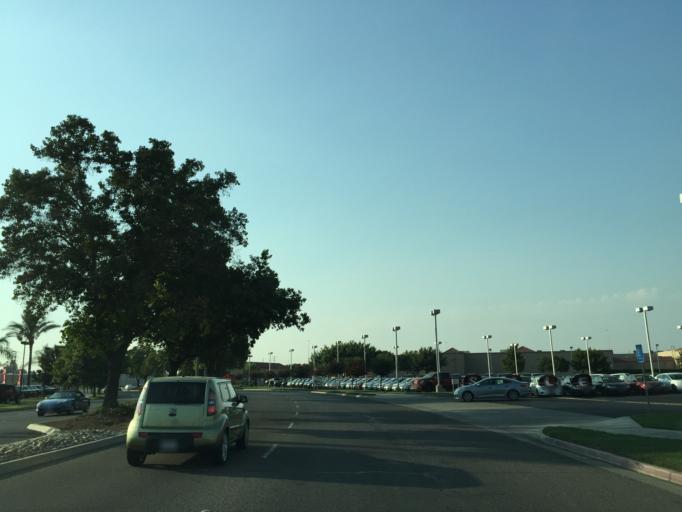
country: US
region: California
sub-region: Tulare County
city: Visalia
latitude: 36.3224
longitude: -119.2766
